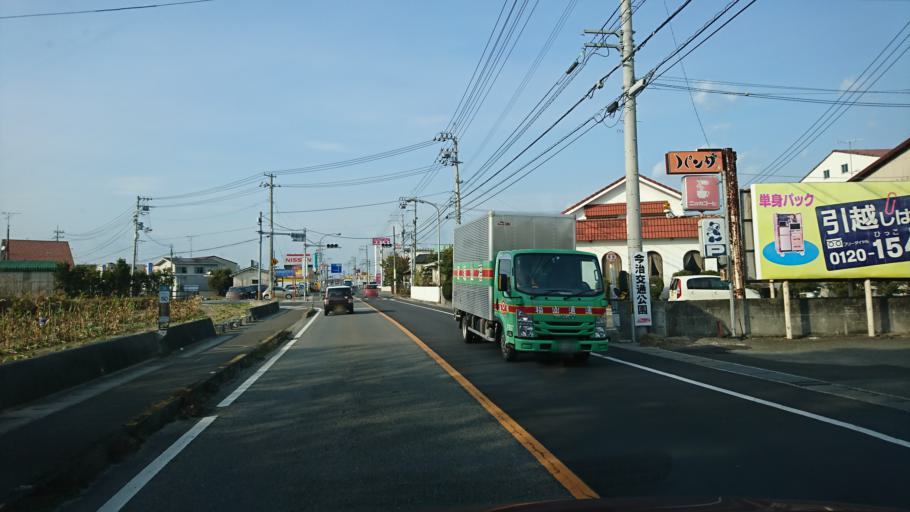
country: JP
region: Ehime
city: Saijo
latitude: 34.0344
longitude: 133.0347
